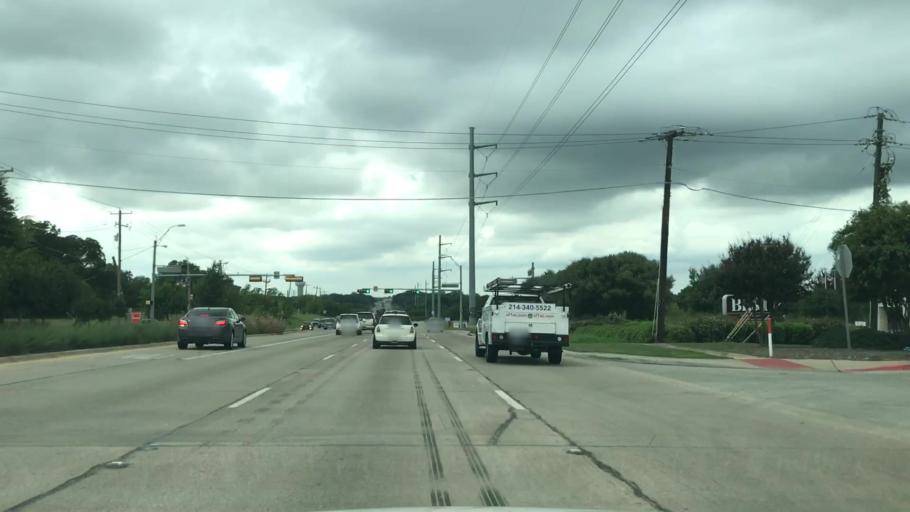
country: US
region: Texas
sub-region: Dallas County
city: Rowlett
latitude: 32.9085
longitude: -96.5835
